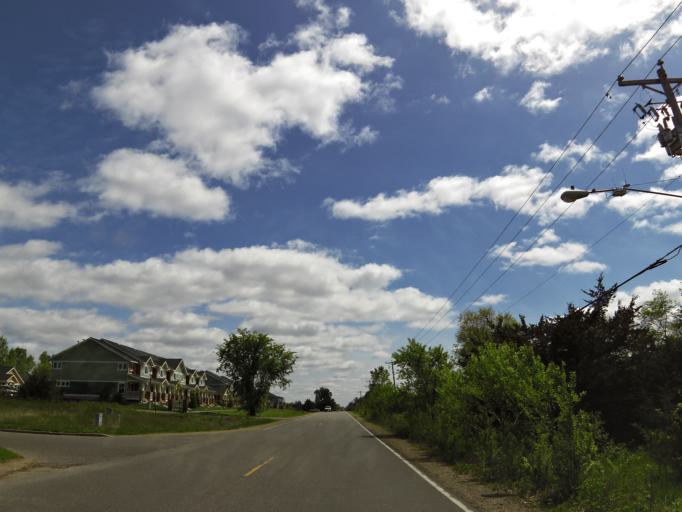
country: US
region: Wisconsin
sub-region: Saint Croix County
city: Hudson
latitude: 44.9570
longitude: -92.7313
